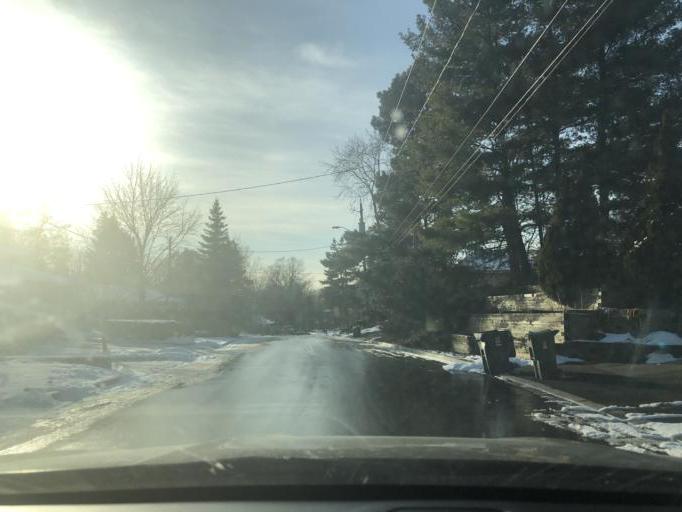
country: CA
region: Ontario
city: Toronto
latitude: 43.6967
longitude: -79.4783
